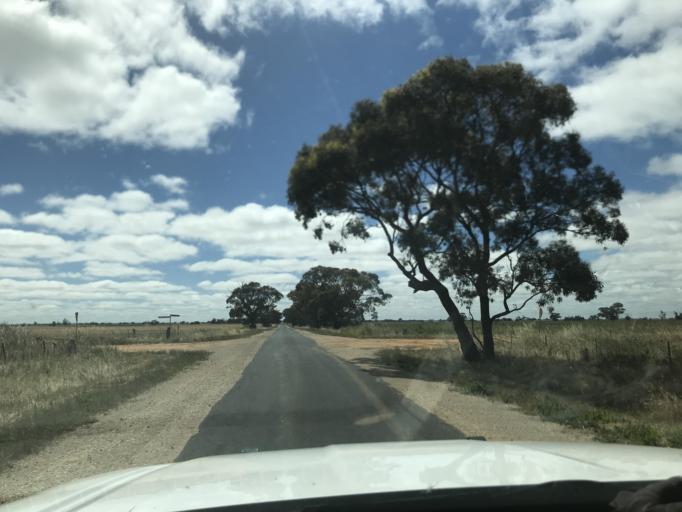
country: AU
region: South Australia
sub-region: Tatiara
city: Bordertown
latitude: -36.2792
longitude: 141.1224
